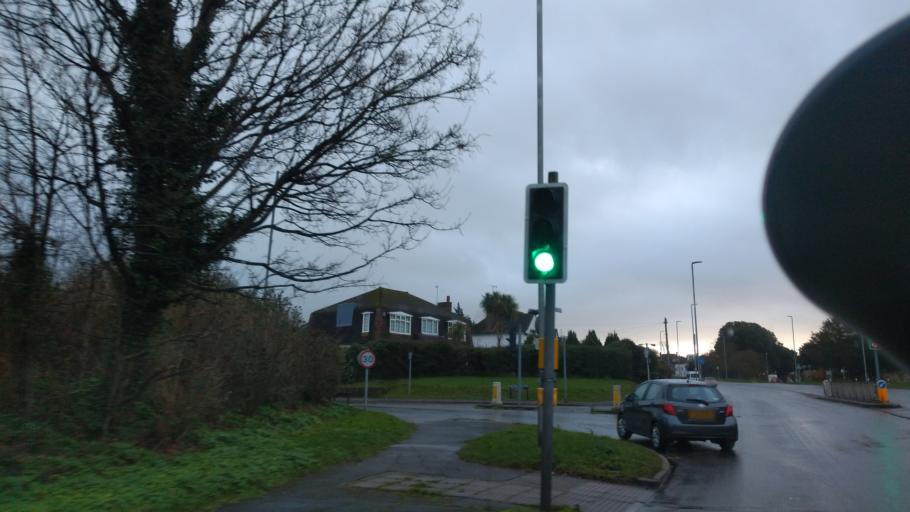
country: GB
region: England
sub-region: East Sussex
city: Eastbourne
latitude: 50.8047
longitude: 0.2495
